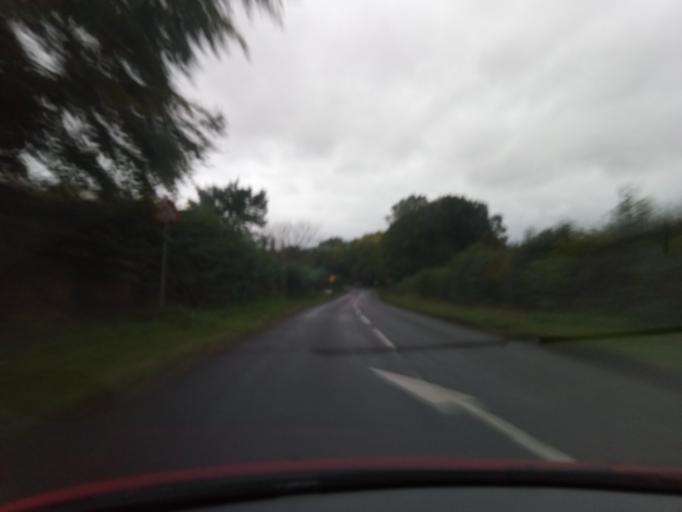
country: GB
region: England
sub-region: Darlington
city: High Coniscliffe
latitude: 54.5318
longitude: -1.6722
